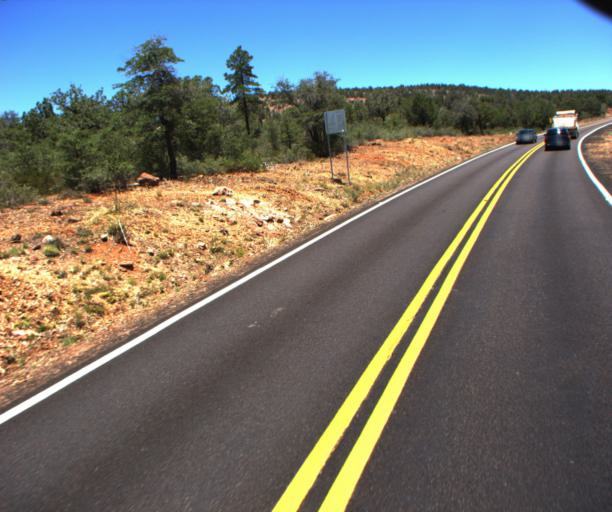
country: US
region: Arizona
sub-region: Gila County
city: Pine
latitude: 34.3436
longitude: -111.4259
